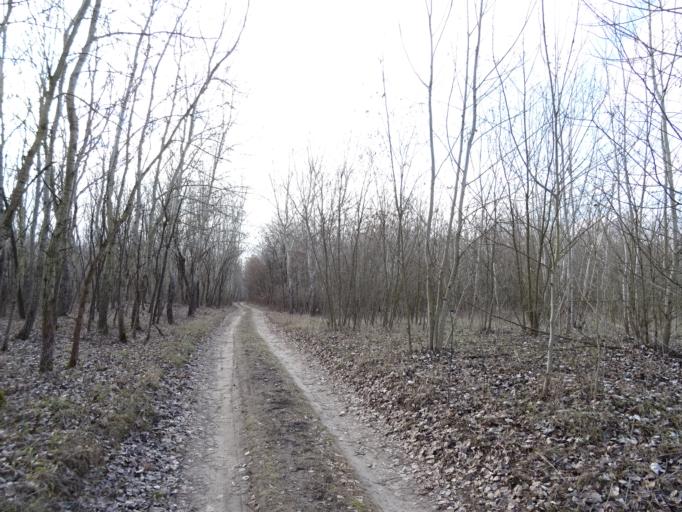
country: HU
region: Bacs-Kiskun
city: Szabadszallas
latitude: 46.8769
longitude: 19.2953
